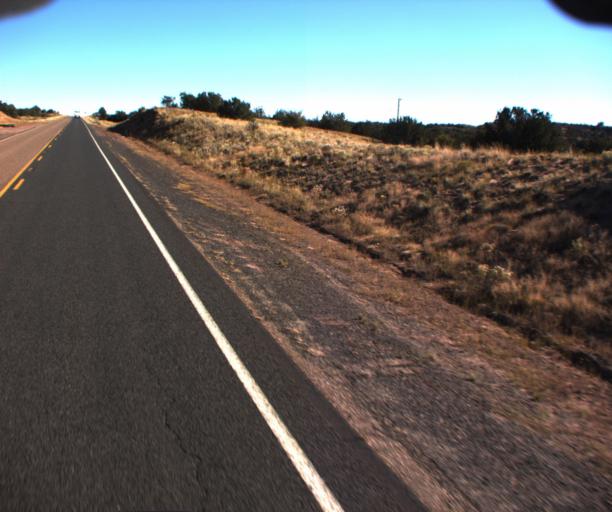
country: US
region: Arizona
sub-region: Apache County
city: Houck
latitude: 35.3527
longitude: -109.4583
